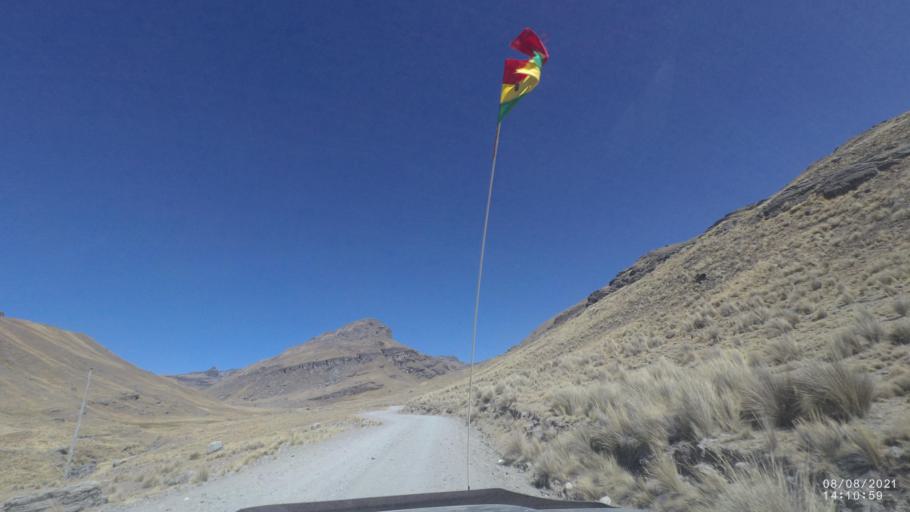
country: BO
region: Cochabamba
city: Sipe Sipe
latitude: -17.1562
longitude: -66.4327
